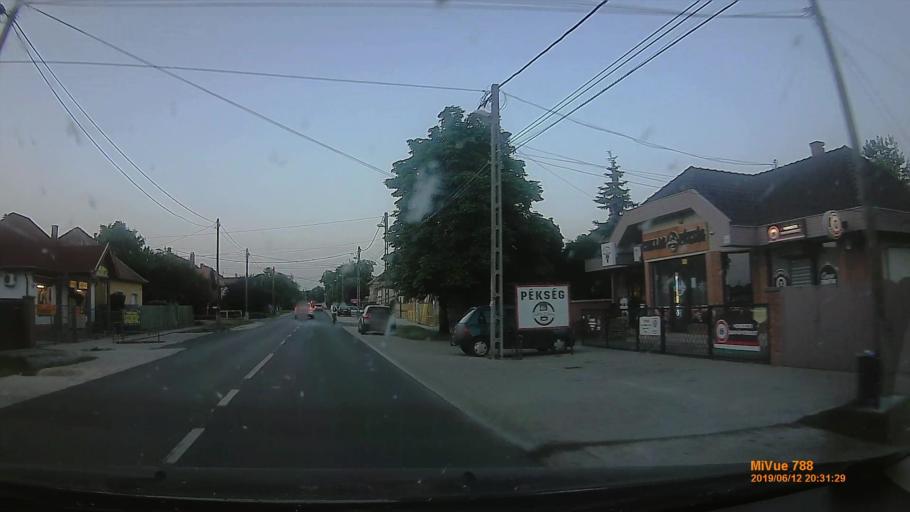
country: HU
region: Pest
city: Vecses
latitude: 47.4045
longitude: 19.2547
